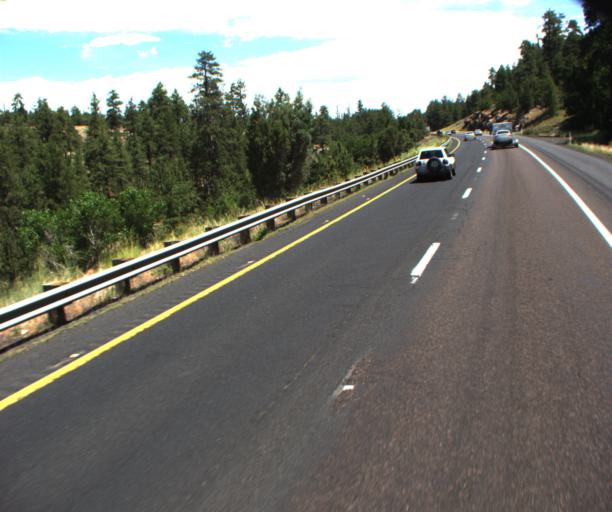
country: US
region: Arizona
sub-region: Coconino County
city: Sedona
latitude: 34.8240
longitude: -111.6102
